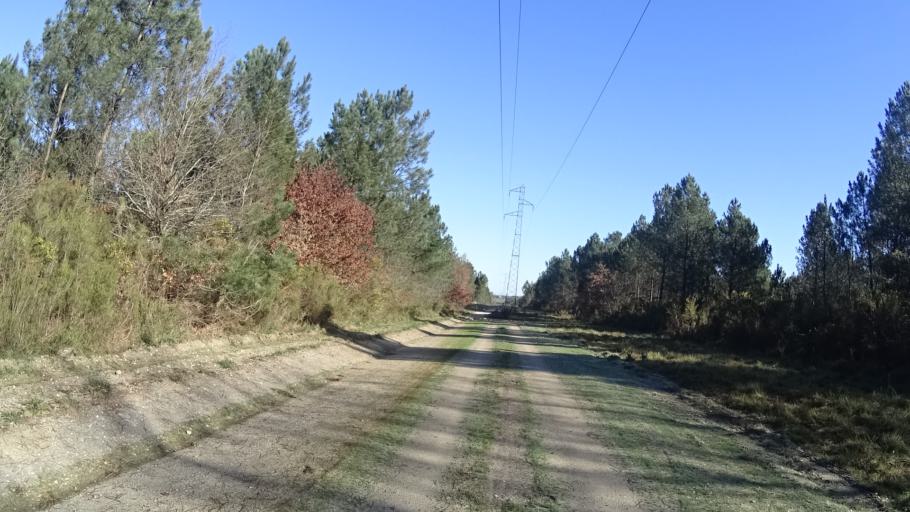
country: FR
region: Aquitaine
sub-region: Departement de la Dordogne
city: La Roche-Chalais
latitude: 45.1695
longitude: 0.0349
